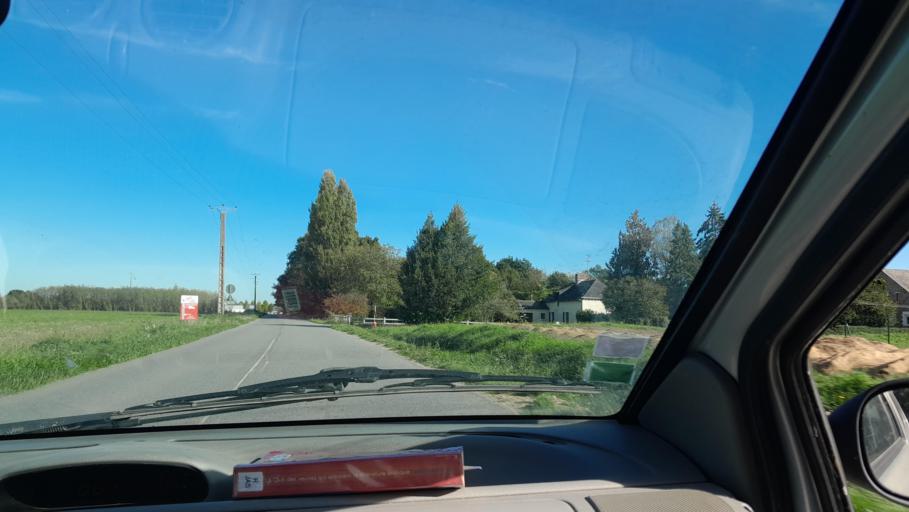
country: FR
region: Brittany
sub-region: Departement d'Ille-et-Vilaine
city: Etrelles
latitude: 48.0564
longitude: -1.1776
